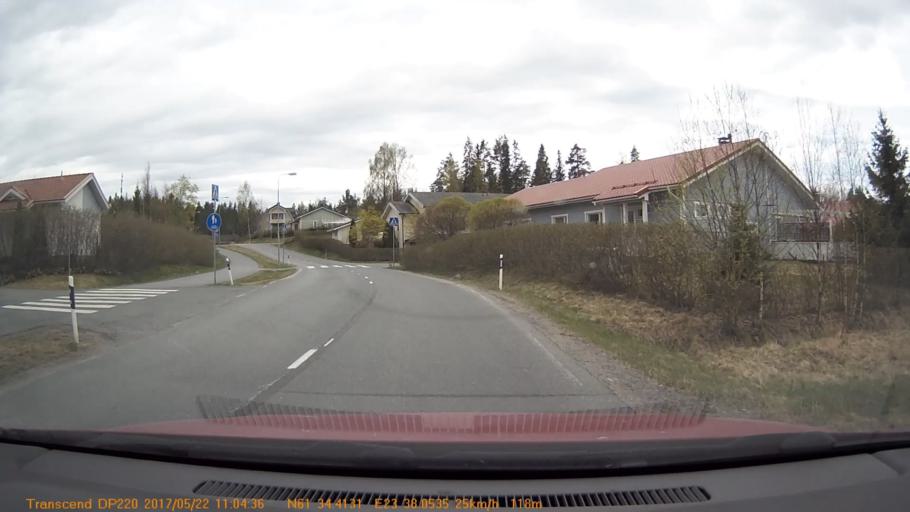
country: FI
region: Pirkanmaa
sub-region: Tampere
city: Yloejaervi
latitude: 61.5736
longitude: 23.6342
